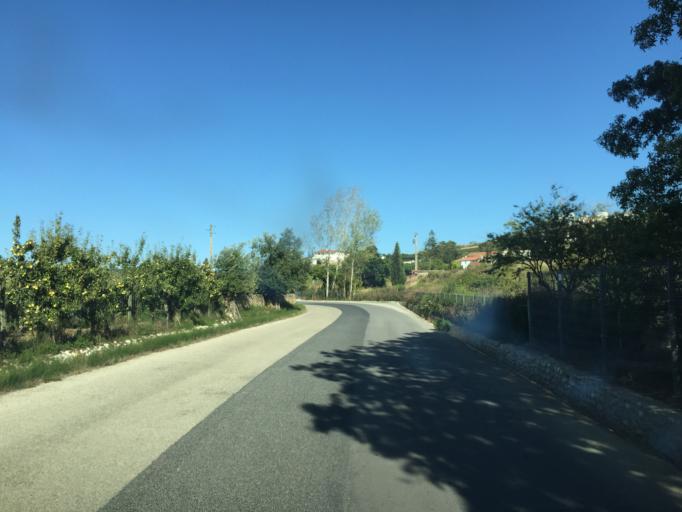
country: PT
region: Lisbon
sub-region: Torres Vedras
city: Torres Vedras
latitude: 39.0947
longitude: -9.2857
